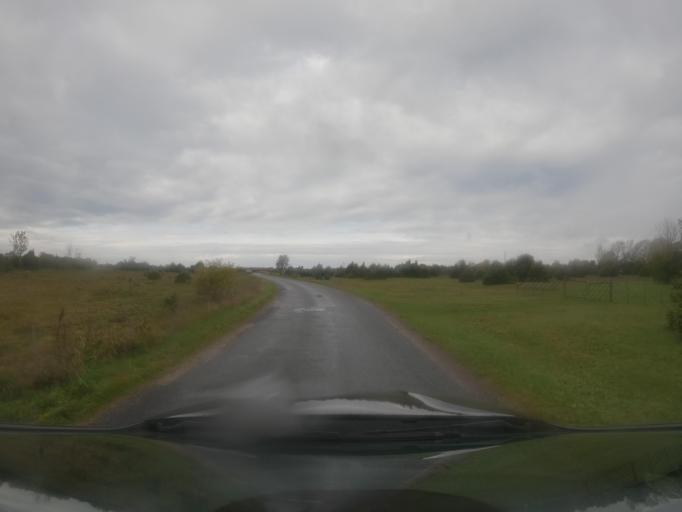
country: EE
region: Saare
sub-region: Kuressaare linn
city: Kuressaare
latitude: 58.4437
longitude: 21.9820
